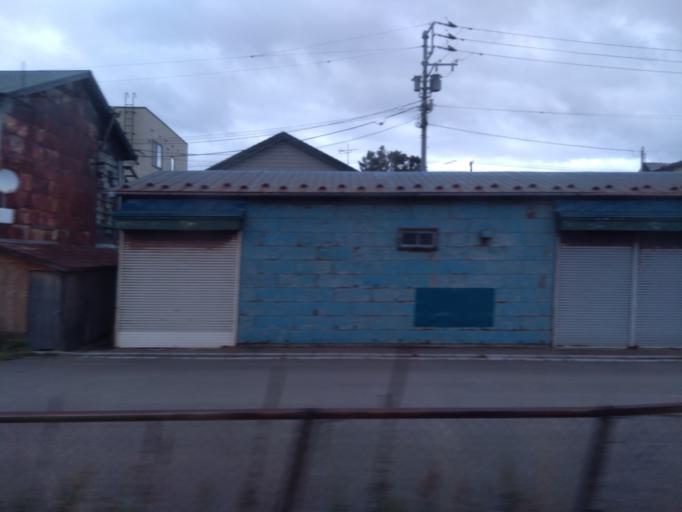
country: JP
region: Hokkaido
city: Hakodate
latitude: 41.7854
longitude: 140.7297
